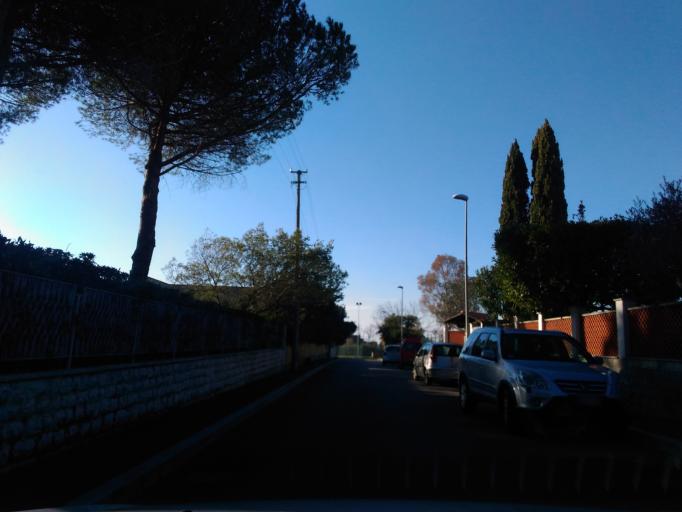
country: IT
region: Tuscany
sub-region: Provincia di Livorno
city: Livorno
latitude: 43.5030
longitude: 10.3366
